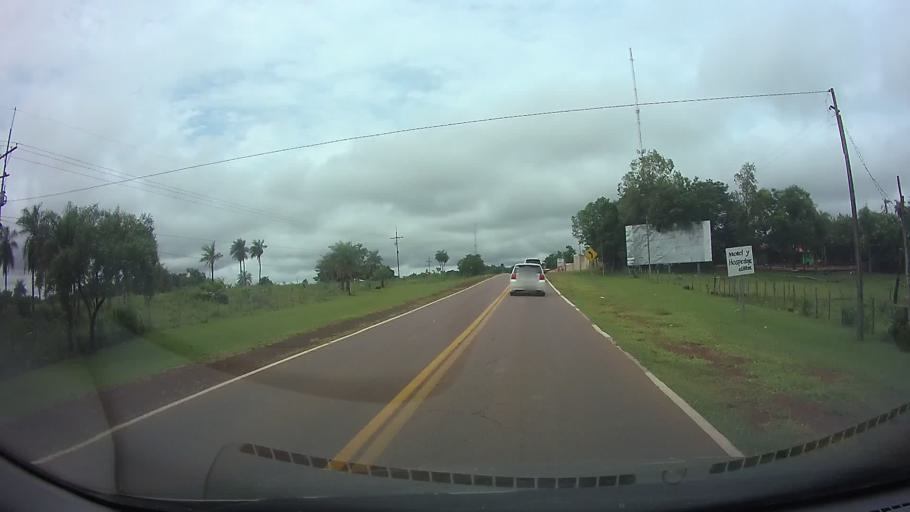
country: PY
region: Paraguari
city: Acahay
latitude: -25.9010
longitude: -57.1168
